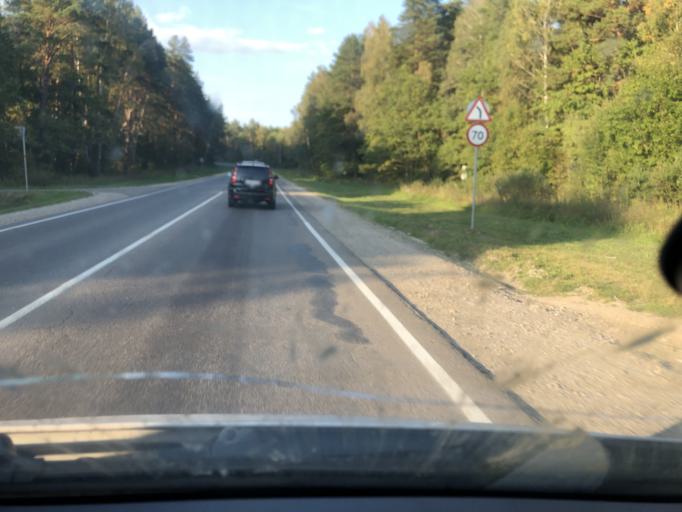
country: RU
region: Kaluga
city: Peremyshl'
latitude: 54.3865
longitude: 36.2040
